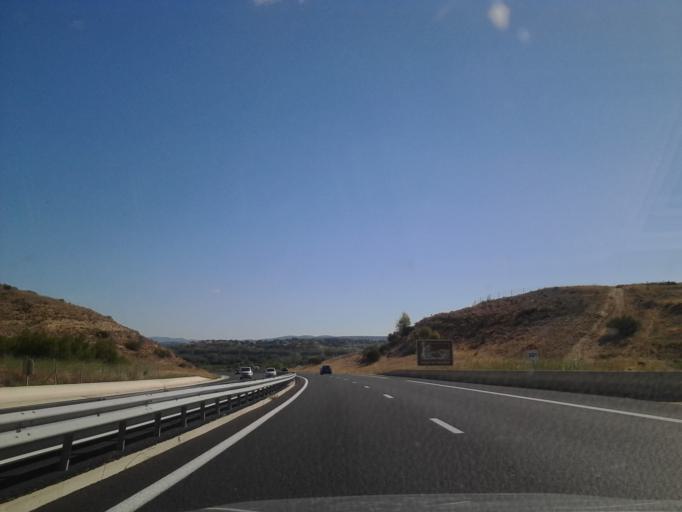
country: FR
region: Languedoc-Roussillon
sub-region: Departement de l'Herault
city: Aspiran
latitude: 43.5560
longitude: 3.4615
